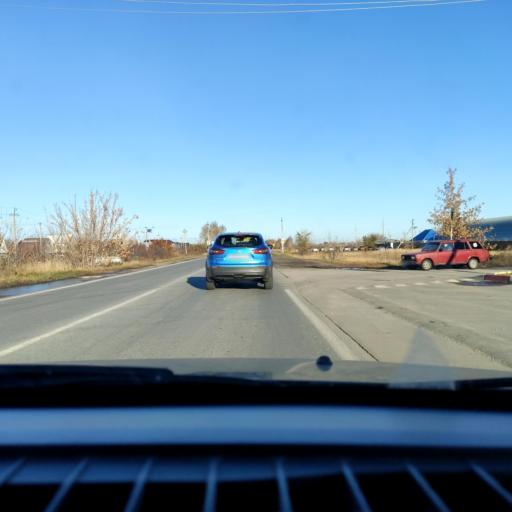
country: RU
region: Samara
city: Tol'yatti
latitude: 53.5753
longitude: 49.3392
